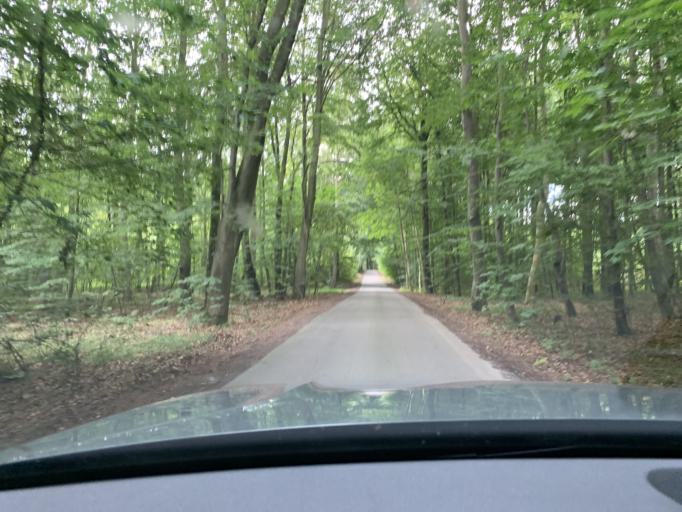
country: DK
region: Zealand
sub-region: Guldborgsund Kommune
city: Norre Alslev
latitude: 54.8495
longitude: 11.9346
